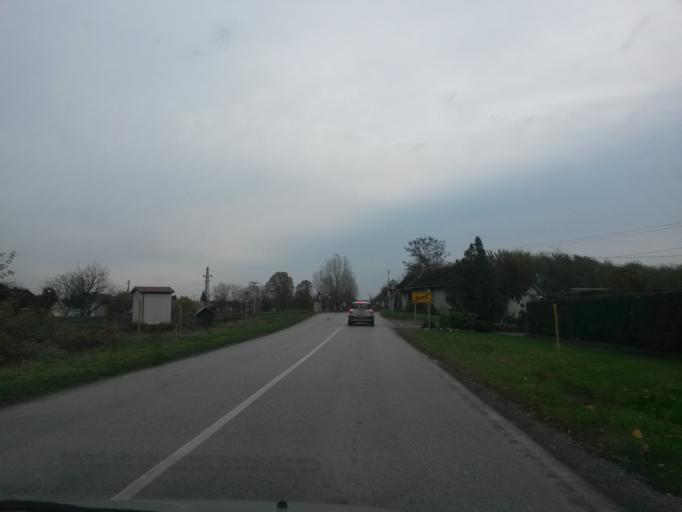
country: HR
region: Osjecko-Baranjska
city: Darda
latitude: 45.6223
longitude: 18.7085
